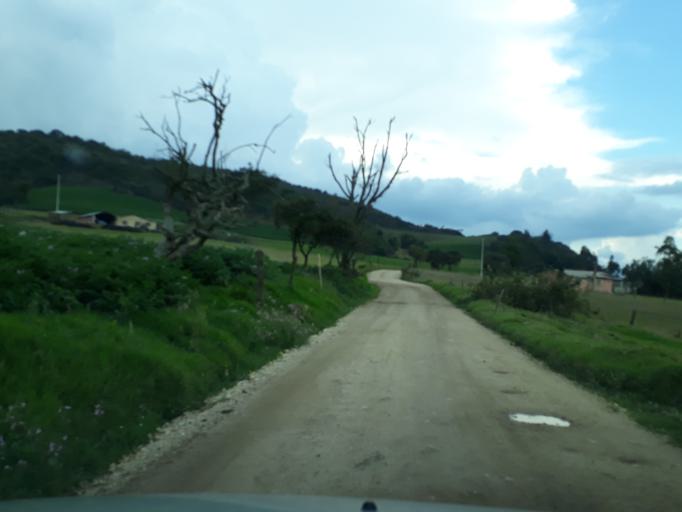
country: CO
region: Cundinamarca
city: Lenguazaque
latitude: 5.2526
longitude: -73.6814
